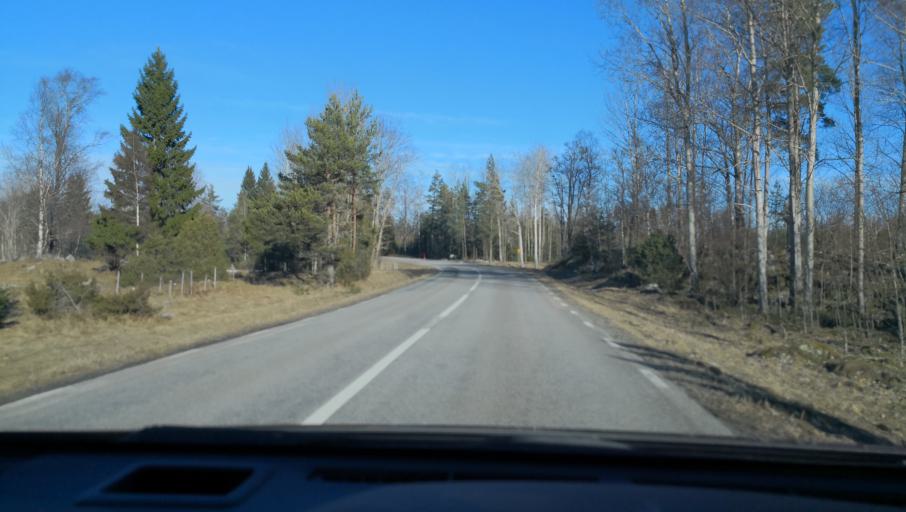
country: SE
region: Uppsala
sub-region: Osthammars Kommun
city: Osterbybruk
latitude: 60.2821
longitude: 17.9766
